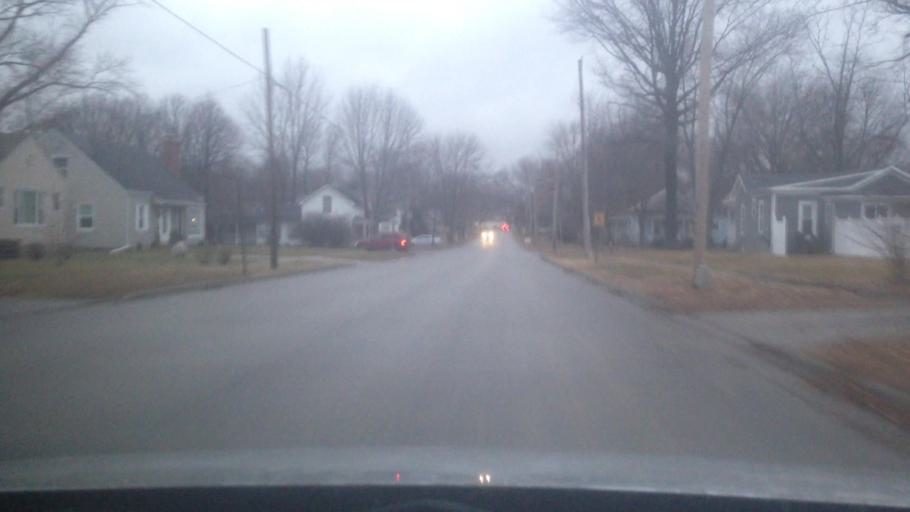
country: US
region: Illinois
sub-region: Christian County
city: Pana
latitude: 39.3832
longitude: -89.0773
